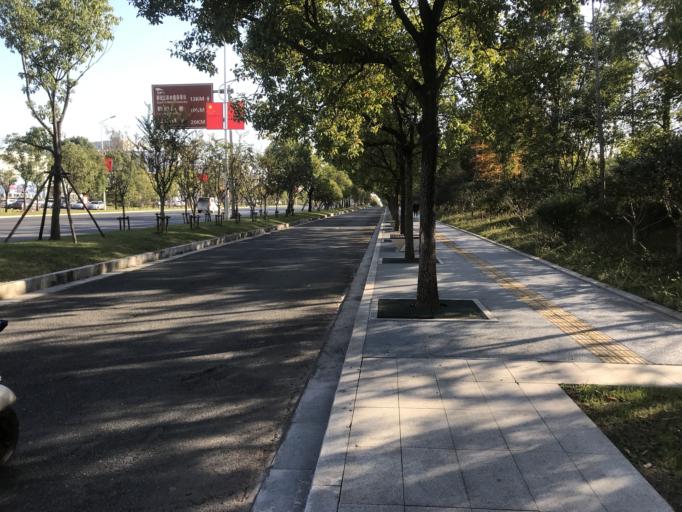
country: CN
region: Anhui Sheng
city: Xintan
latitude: 29.7714
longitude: 118.2587
